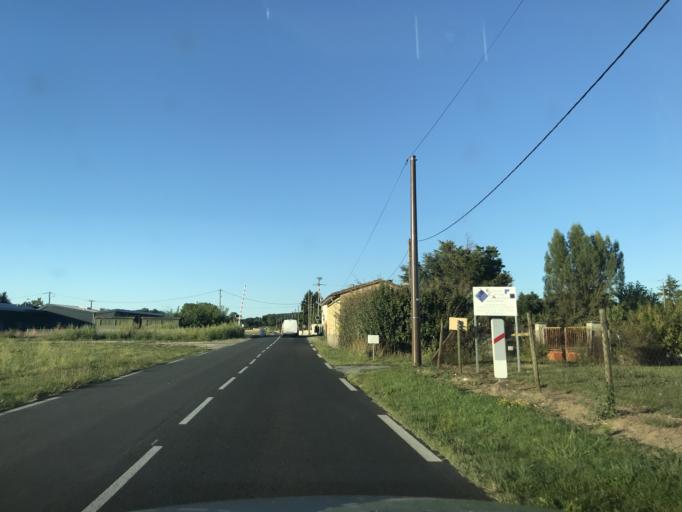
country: FR
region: Aquitaine
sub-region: Departement de la Gironde
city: Mouliets-et-Villemartin
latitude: 44.8591
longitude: -0.0573
